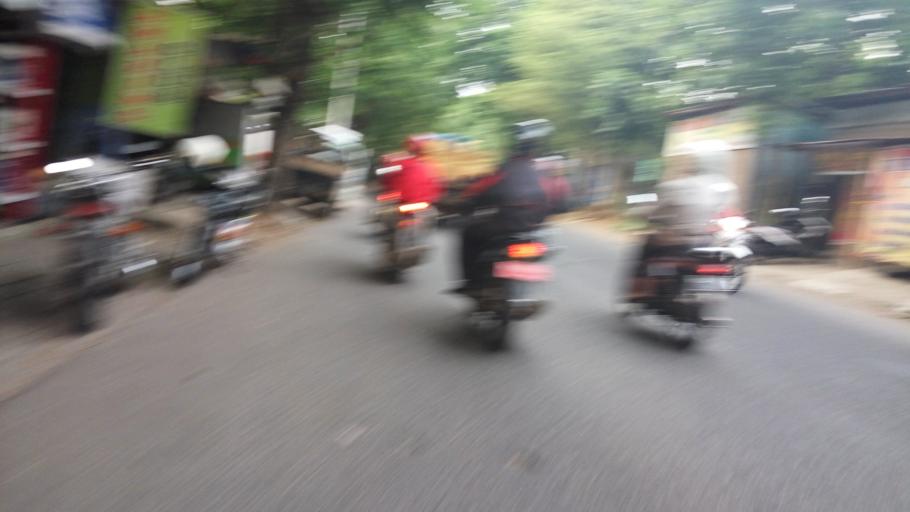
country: ID
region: Central Java
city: Semarang
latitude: -6.9995
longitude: 110.3969
